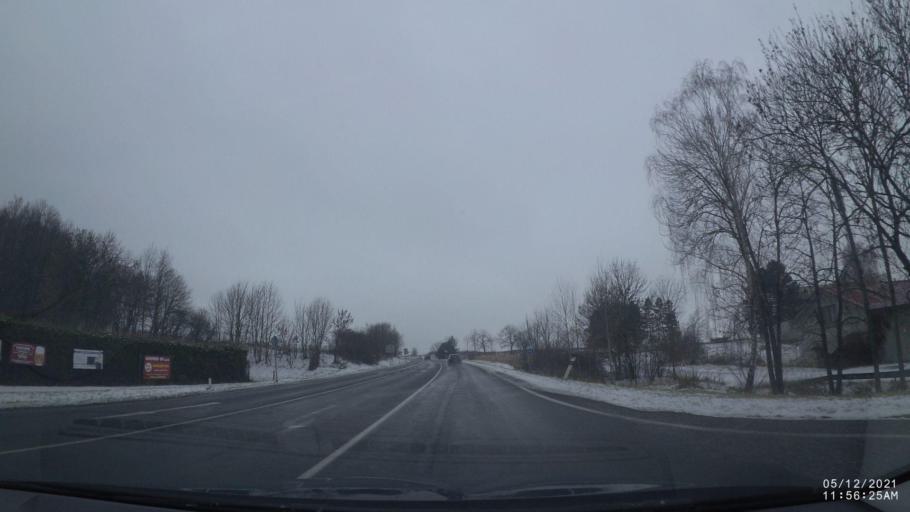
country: CZ
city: Dobruska
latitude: 50.2828
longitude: 16.1506
